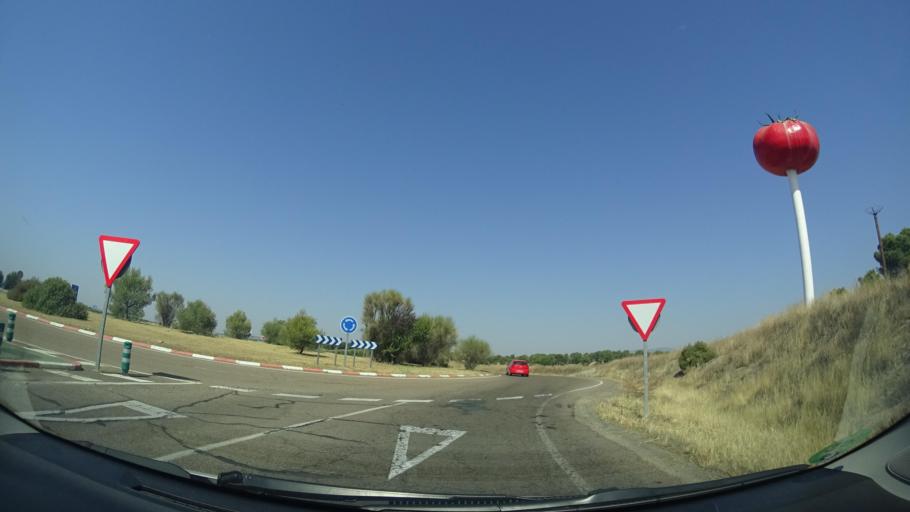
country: ES
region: Extremadura
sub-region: Provincia de Caceres
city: Miajadas
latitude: 39.1354
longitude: -5.9464
